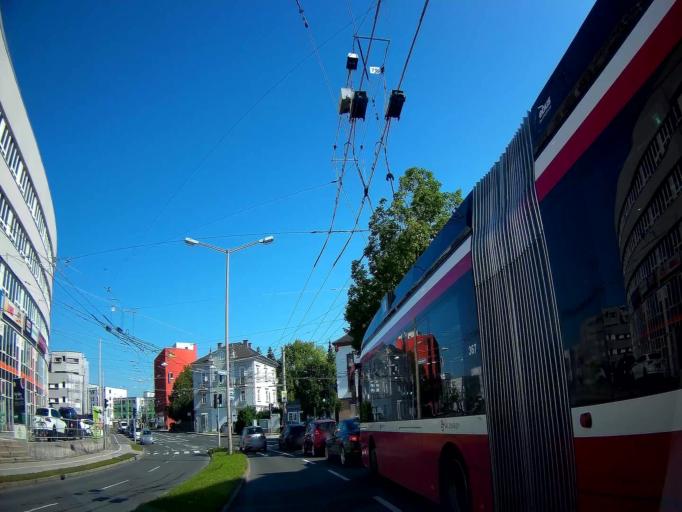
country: IT
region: Tuscany
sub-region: Provincia di Siena
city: Chianciano Terme
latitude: 43.0277
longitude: 11.7592
